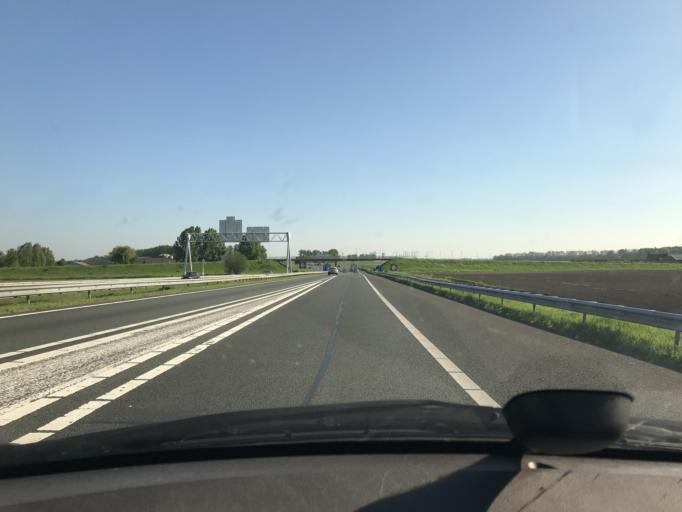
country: NL
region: North Brabant
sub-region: Gemeente Woensdrecht
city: Woensdrecht
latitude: 51.4277
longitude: 4.2763
